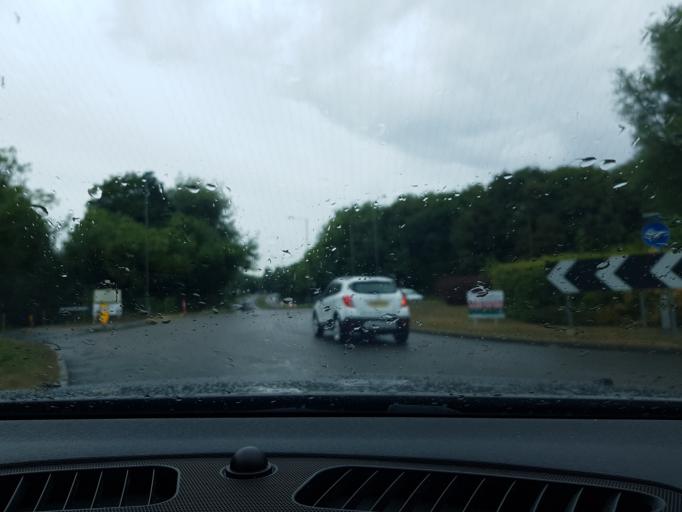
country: GB
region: England
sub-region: Surrey
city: Hale
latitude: 51.2217
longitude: -0.7786
